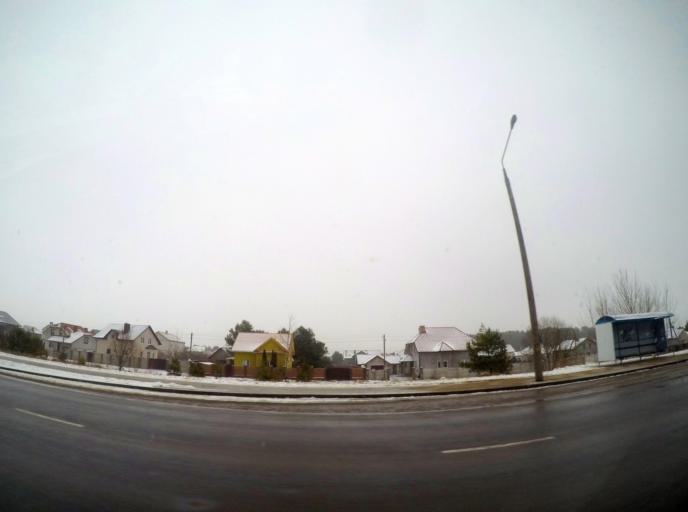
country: BY
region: Grodnenskaya
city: Hrodna
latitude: 53.6183
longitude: 23.8218
